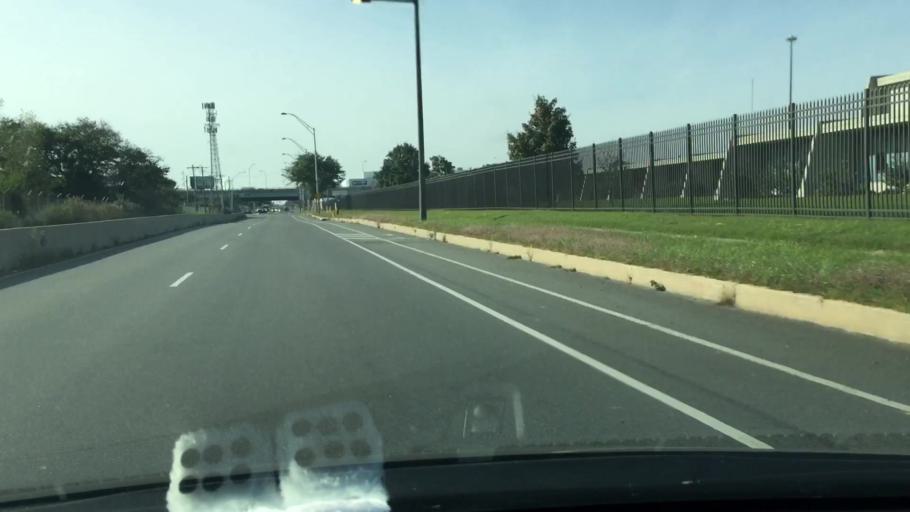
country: US
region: New Jersey
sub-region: Camden County
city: Gloucester City
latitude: 39.9020
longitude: -75.1469
